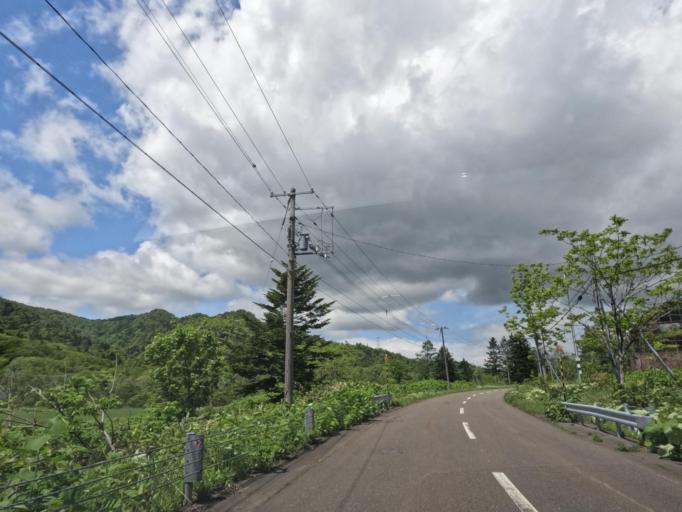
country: JP
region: Hokkaido
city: Tobetsu
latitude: 43.4389
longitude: 141.5822
